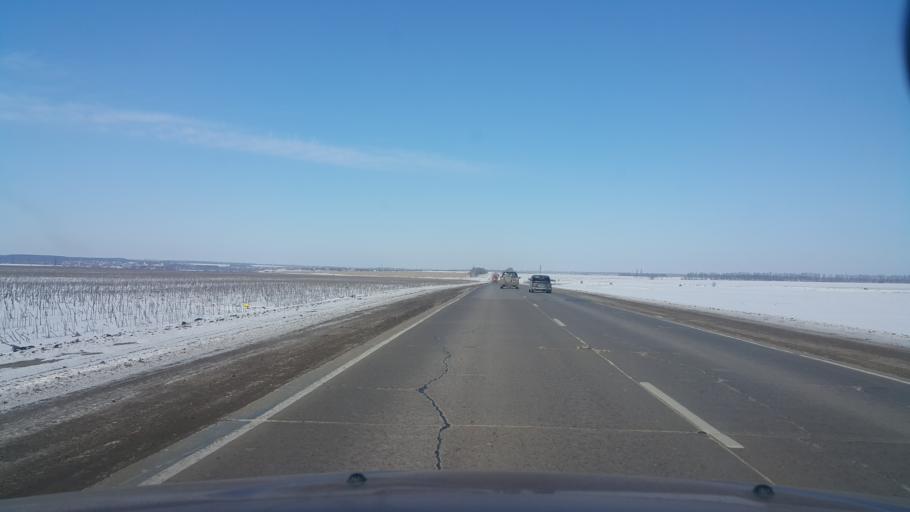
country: RU
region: Tambov
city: Pokrovo-Prigorodnoye
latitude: 52.6218
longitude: 41.3429
